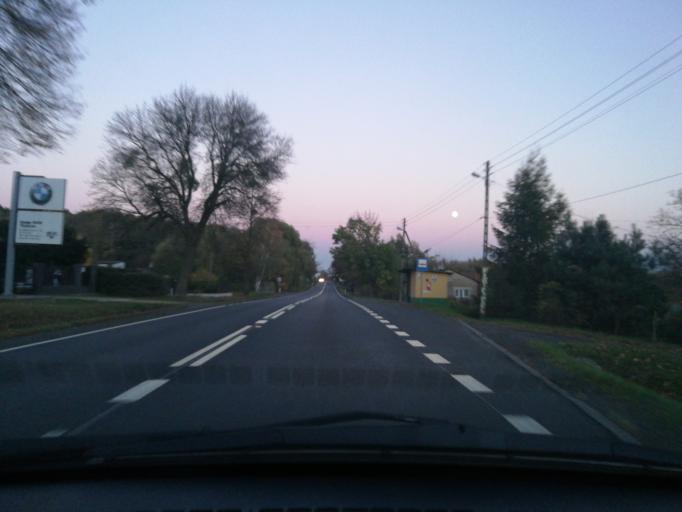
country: PL
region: Lodz Voivodeship
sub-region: Powiat brzezinski
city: Brzeziny
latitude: 51.8044
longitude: 19.6926
